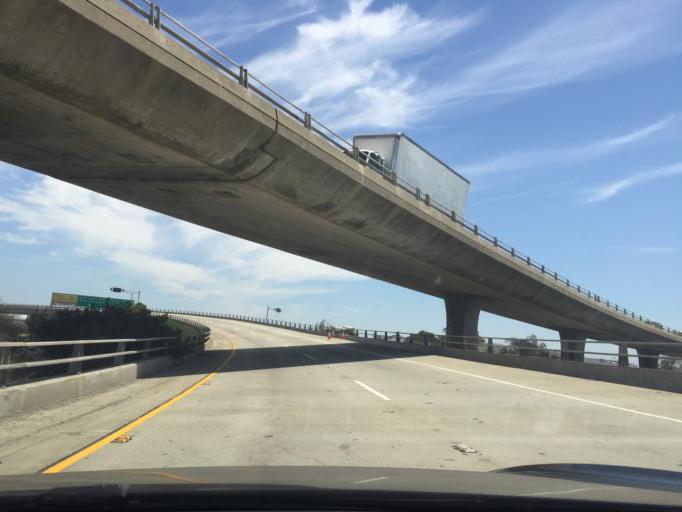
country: US
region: California
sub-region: San Mateo County
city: San Bruno
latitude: 37.6344
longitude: -122.4056
